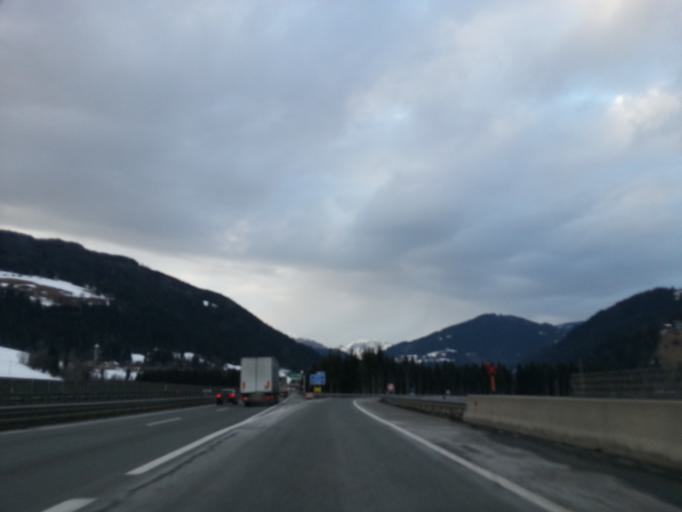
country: AT
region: Salzburg
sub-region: Politischer Bezirk Sankt Johann im Pongau
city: Eben im Pongau
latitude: 47.3894
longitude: 13.4000
